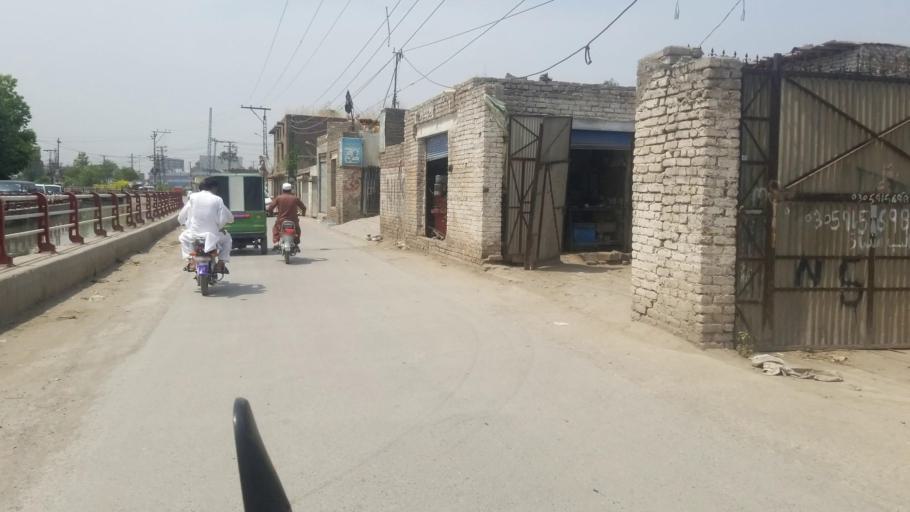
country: PK
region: Khyber Pakhtunkhwa
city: Peshawar
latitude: 34.0155
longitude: 71.6065
